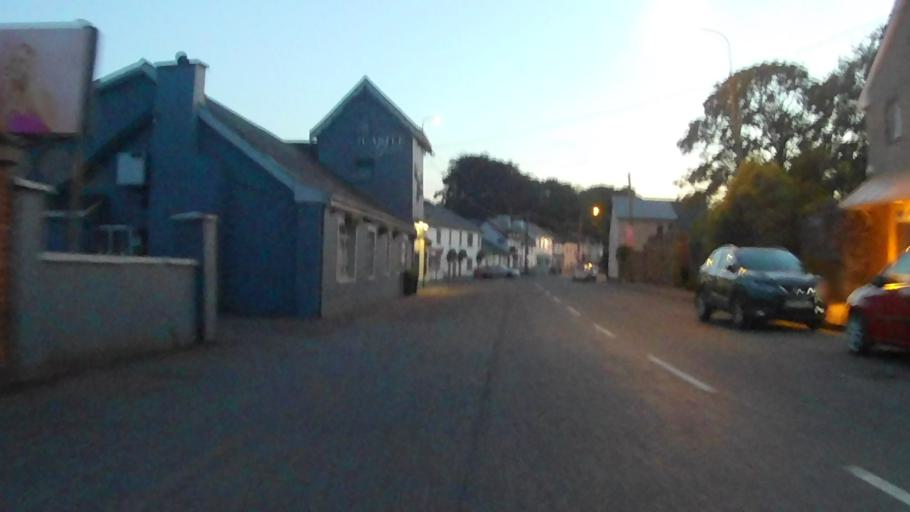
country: IE
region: Munster
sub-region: County Cork
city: Passage West
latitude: 51.9287
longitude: -8.3889
